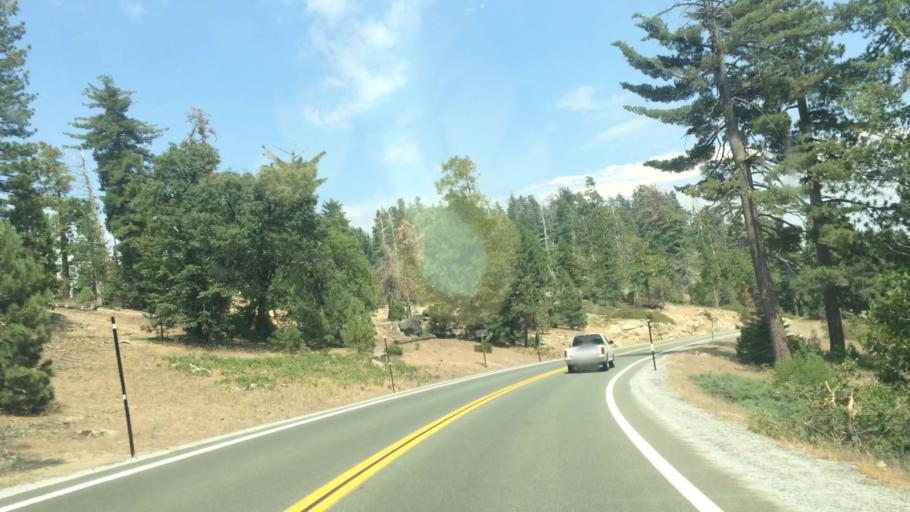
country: US
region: California
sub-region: Amador County
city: Pioneer
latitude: 38.5454
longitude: -120.3377
